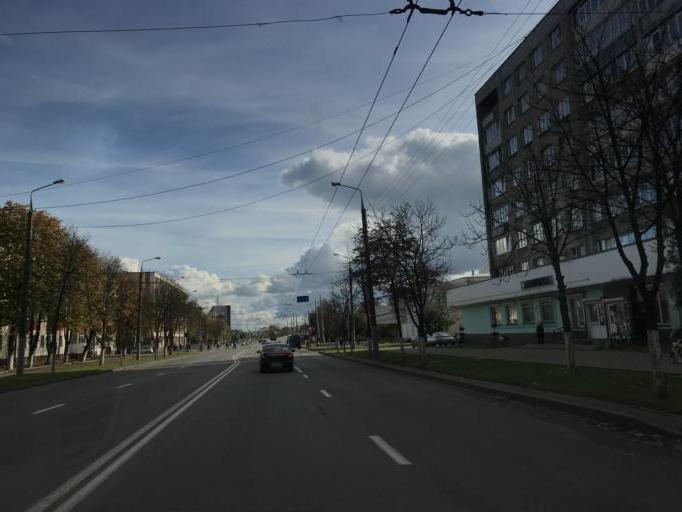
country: BY
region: Gomel
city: Gomel
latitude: 52.4495
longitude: 30.9676
